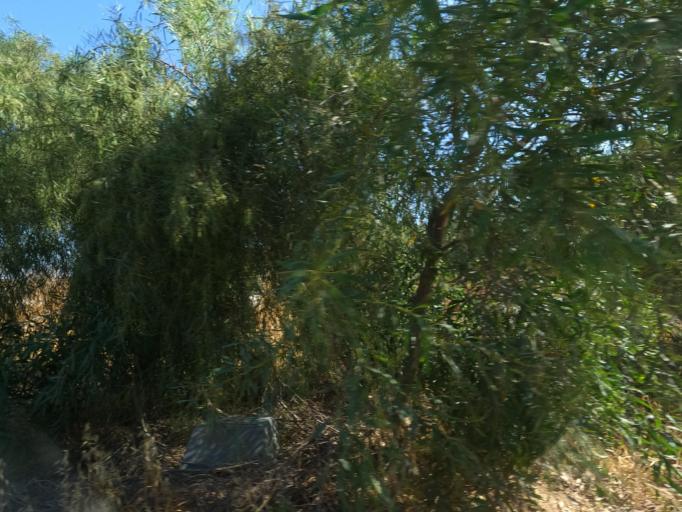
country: CY
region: Ammochostos
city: Frenaros
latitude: 35.0392
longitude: 33.9357
